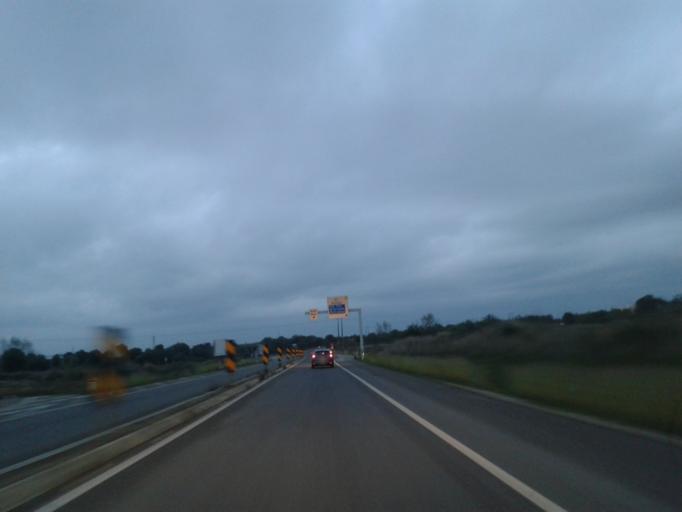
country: PT
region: Faro
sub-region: Albufeira
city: Ferreiras
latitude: 37.1256
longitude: -8.2545
